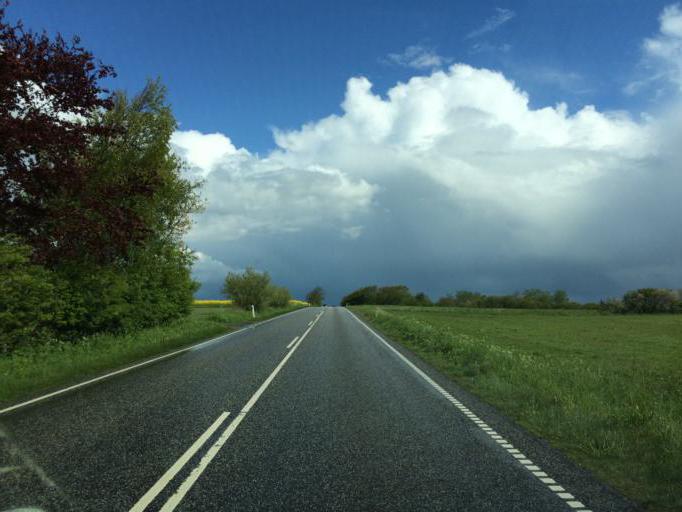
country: DK
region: Central Jutland
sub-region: Holstebro Kommune
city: Vinderup
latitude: 56.4263
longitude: 8.7093
